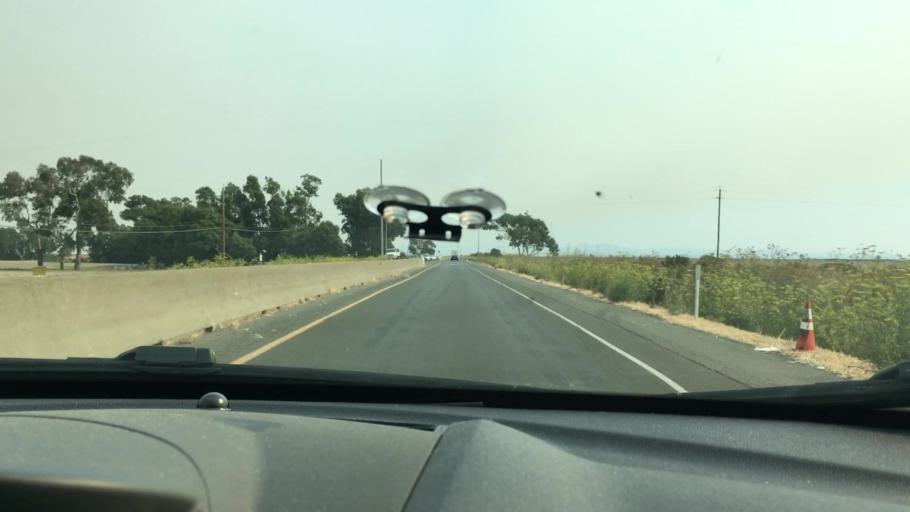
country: US
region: California
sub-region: Marin County
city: Black Point-Green Point
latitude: 38.1546
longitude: -122.4240
